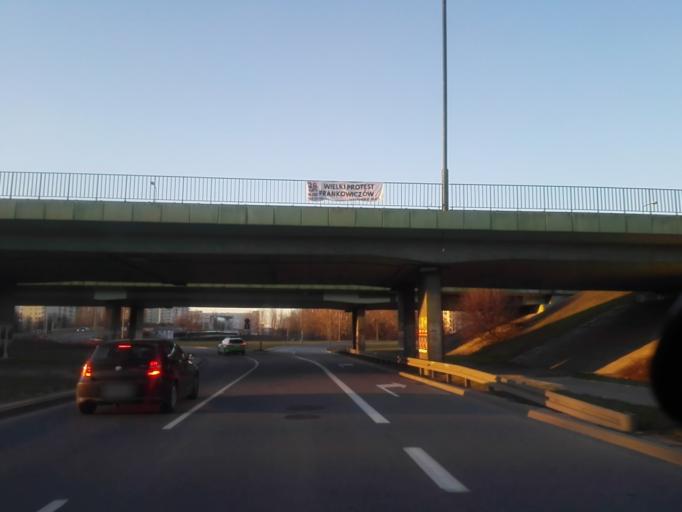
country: PL
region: Masovian Voivodeship
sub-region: Warszawa
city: Ursynow
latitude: 52.1658
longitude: 21.0275
